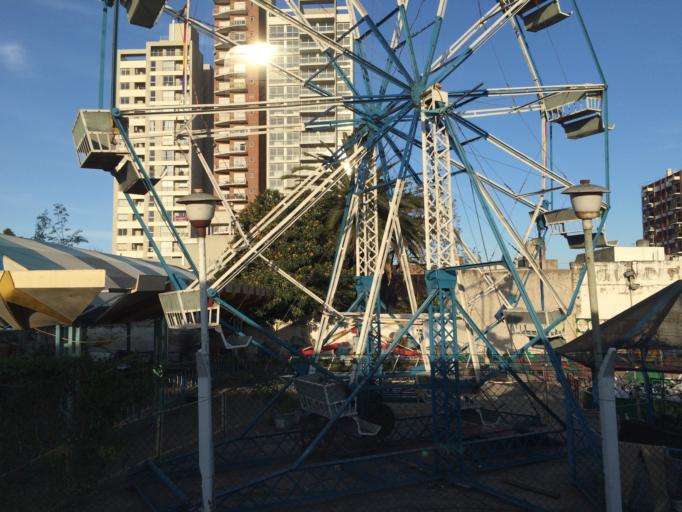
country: AR
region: Buenos Aires
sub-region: Partido de Lomas de Zamora
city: Lomas de Zamora
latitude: -34.7595
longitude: -58.3970
